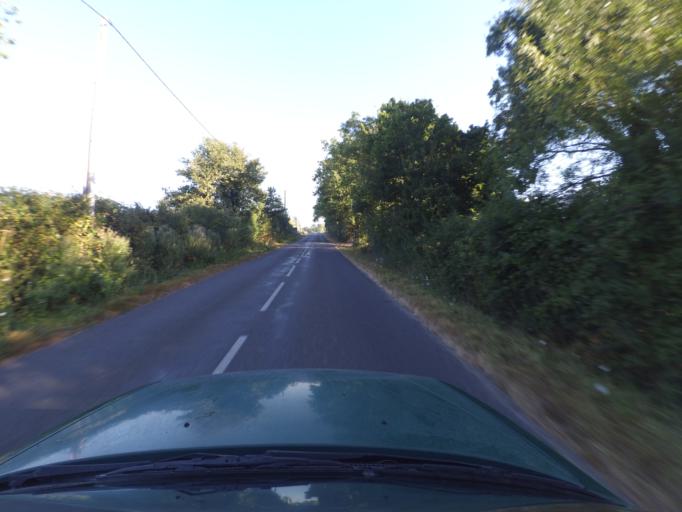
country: FR
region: Pays de la Loire
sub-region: Departement de la Loire-Atlantique
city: Montbert
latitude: 47.0510
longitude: -1.4832
